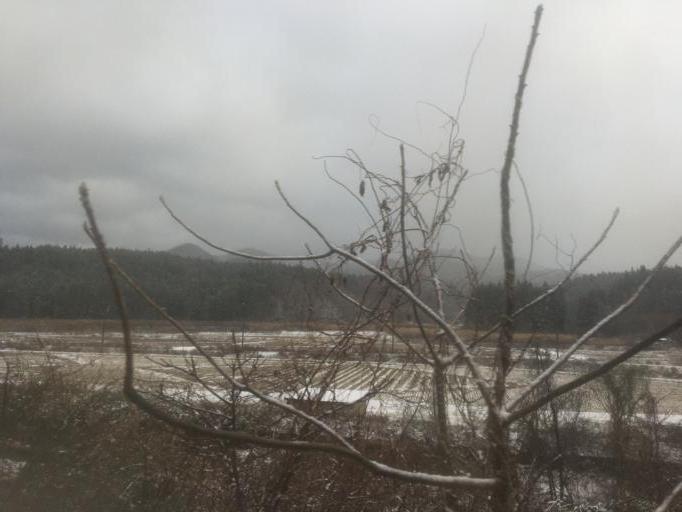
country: JP
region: Aomori
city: Goshogawara
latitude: 41.1382
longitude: 140.5180
